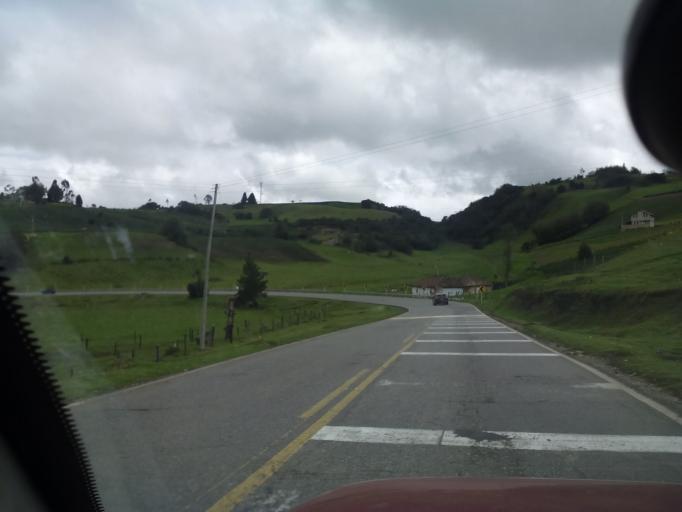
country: CO
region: Boyaca
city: Combita
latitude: 5.6567
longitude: -73.3528
